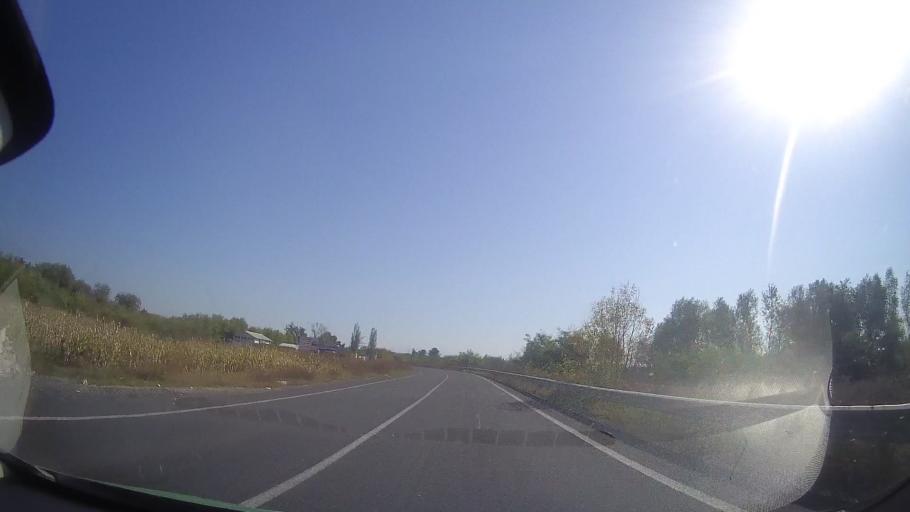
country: RO
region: Timis
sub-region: Comuna Costeiu
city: Costeiu
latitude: 45.7376
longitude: 21.8457
